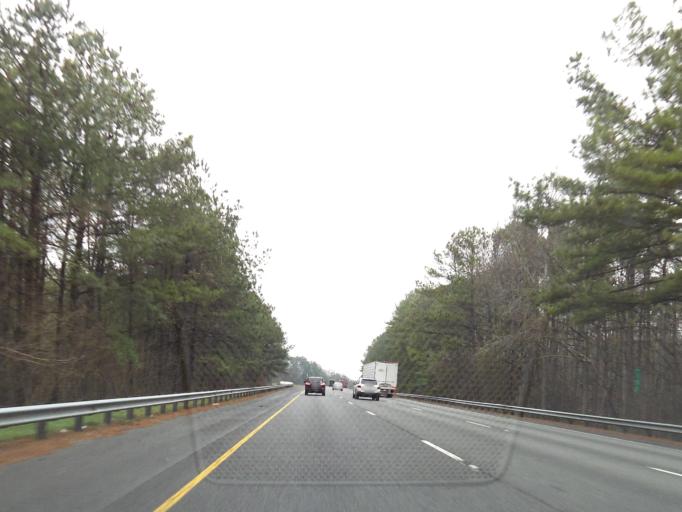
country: US
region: Georgia
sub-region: Monroe County
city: Forsyth
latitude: 33.0918
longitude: -83.9959
